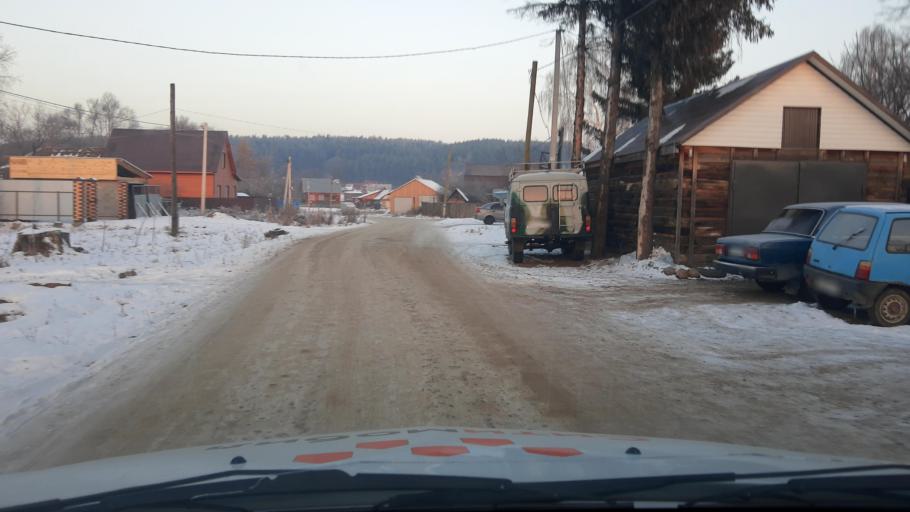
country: RU
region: Bashkortostan
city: Iglino
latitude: 54.8346
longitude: 56.4040
